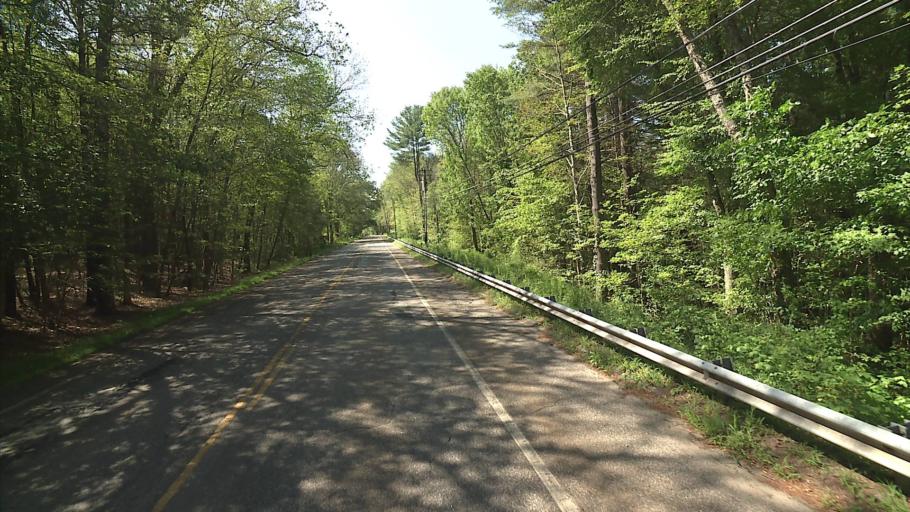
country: US
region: Connecticut
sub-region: Tolland County
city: Storrs
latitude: 41.9012
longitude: -72.1692
